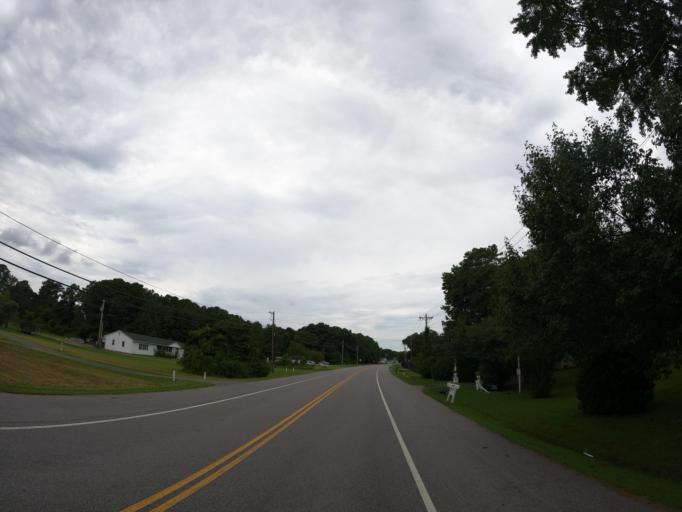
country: US
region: Maryland
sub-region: Saint Mary's County
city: Lexington Park
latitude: 38.1439
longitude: -76.5096
